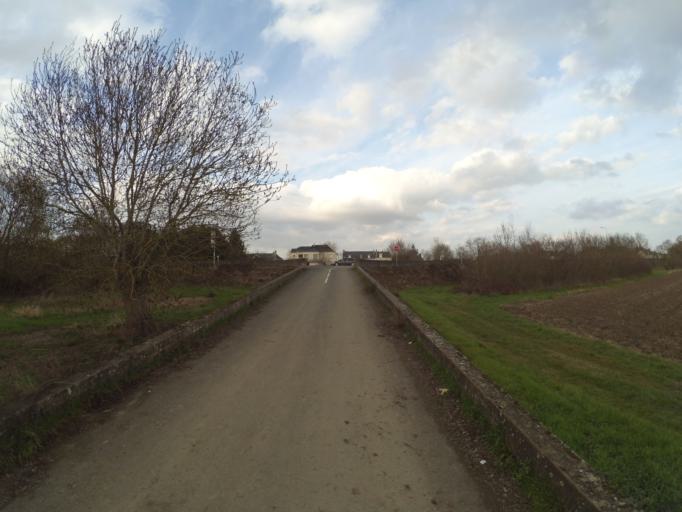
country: FR
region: Pays de la Loire
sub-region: Departement de Maine-et-Loire
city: La Dagueniere
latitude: 47.4180
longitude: -0.4328
